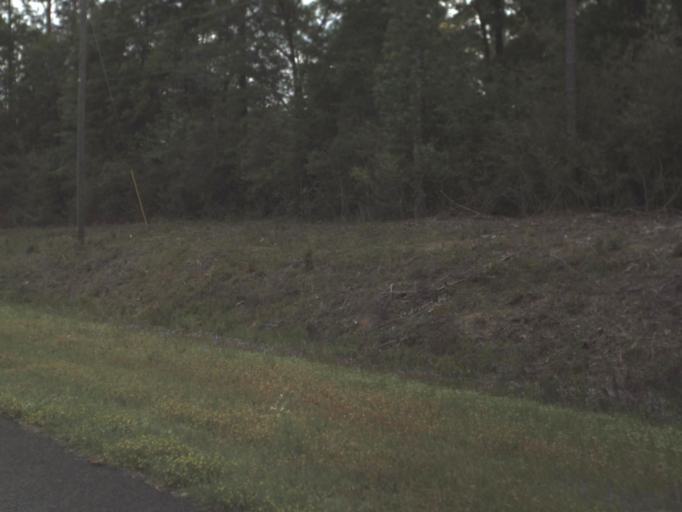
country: US
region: Florida
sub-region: Escambia County
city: Molino
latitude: 30.7834
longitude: -87.3358
